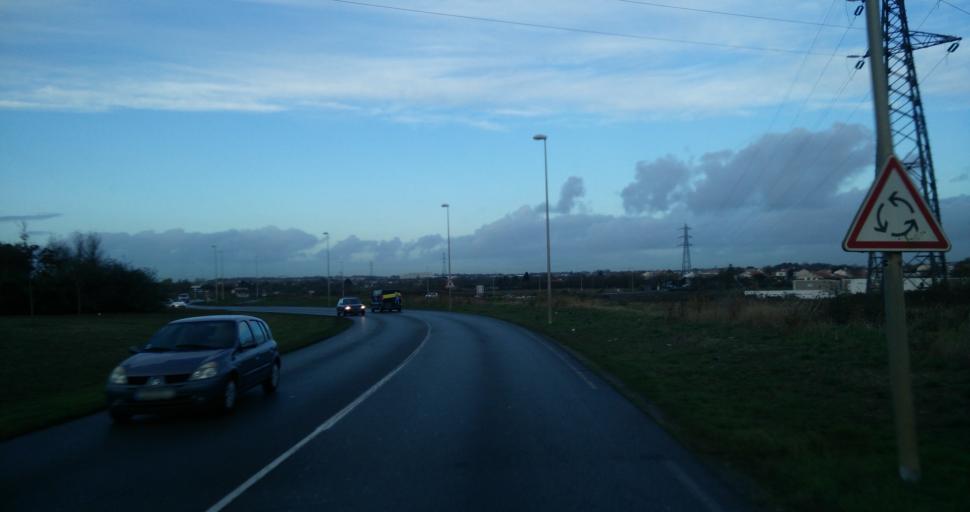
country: FR
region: Poitou-Charentes
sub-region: Departement de la Charente-Maritime
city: Puilboreau
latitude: 46.1793
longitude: -1.1209
